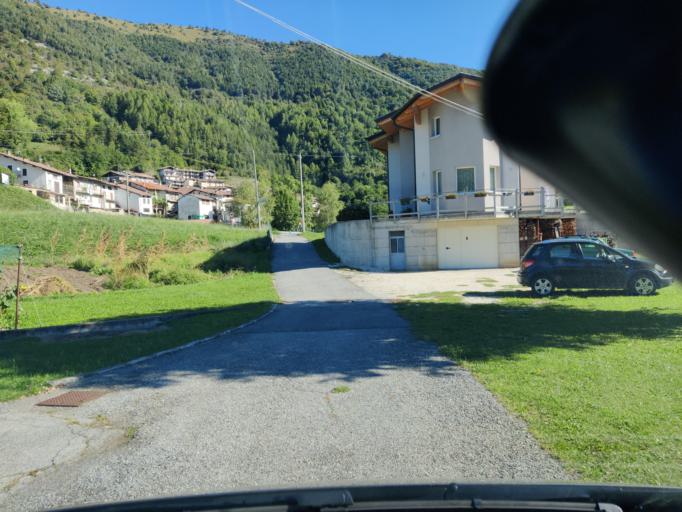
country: IT
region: Lombardy
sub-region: Provincia di Brescia
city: Capovalle
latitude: 45.7525
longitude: 10.5476
